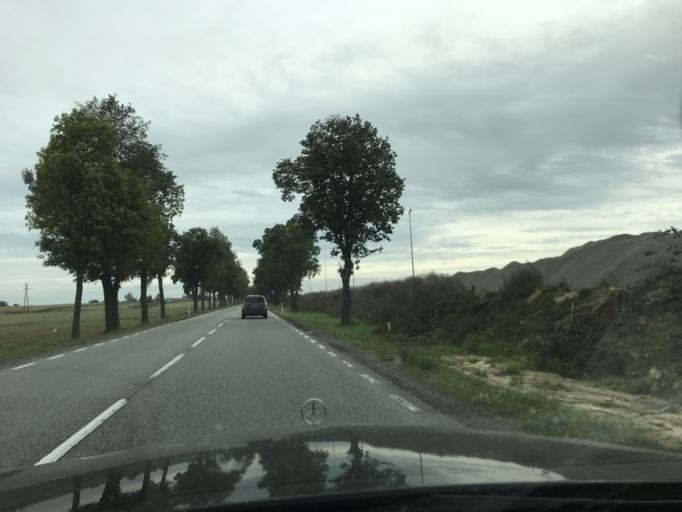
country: PL
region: Lublin Voivodeship
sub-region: Powiat krasnicki
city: Szastarka
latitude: 50.8400
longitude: 22.2992
